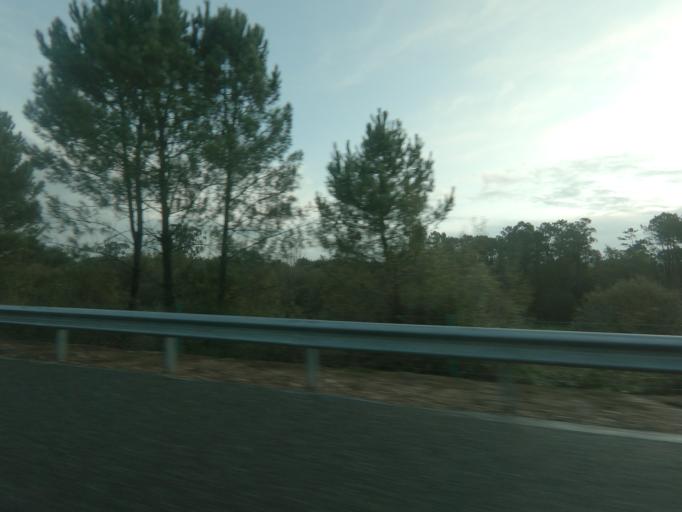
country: ES
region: Galicia
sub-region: Provincia de Pontevedra
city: Tui
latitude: 42.0857
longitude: -8.6396
